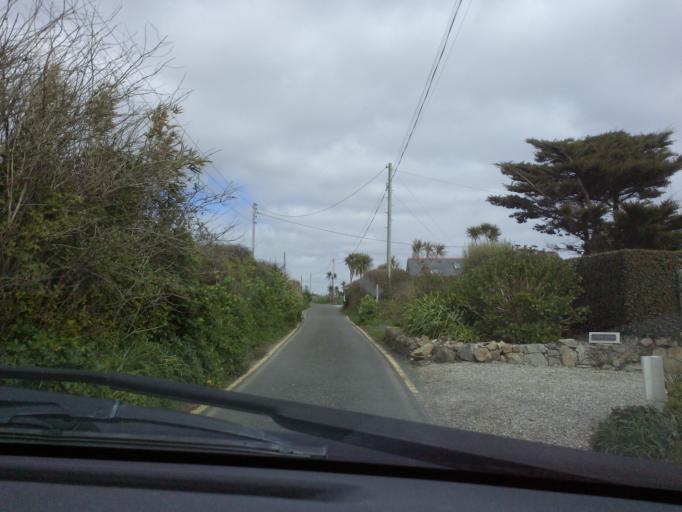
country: GB
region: England
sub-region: Cornwall
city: St. Buryan
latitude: 50.0416
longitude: -5.6558
